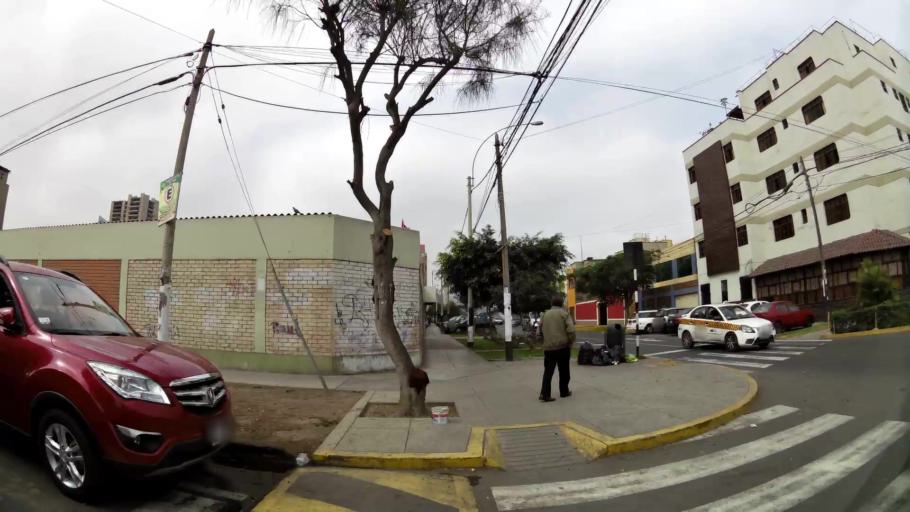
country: PE
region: Lima
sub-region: Lima
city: San Isidro
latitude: -12.0813
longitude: -77.0394
